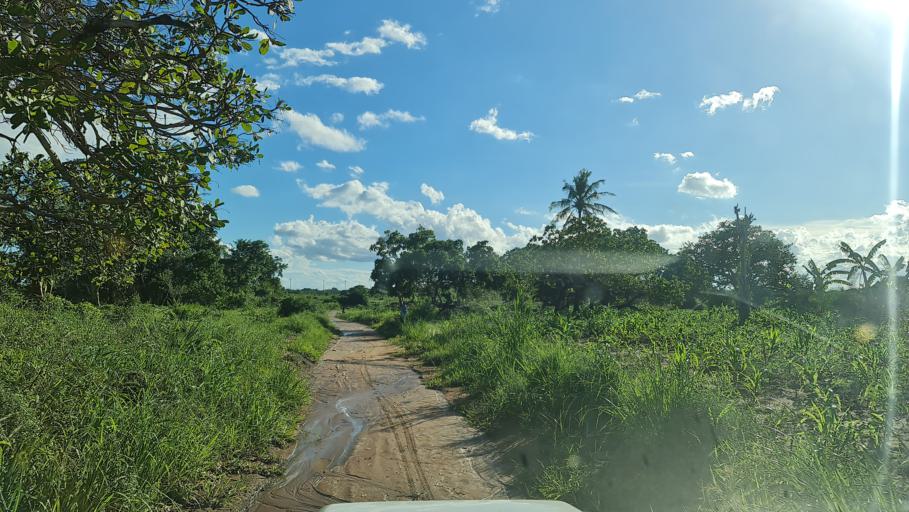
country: MZ
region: Nampula
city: Ilha de Mocambique
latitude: -14.9323
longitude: 40.2144
